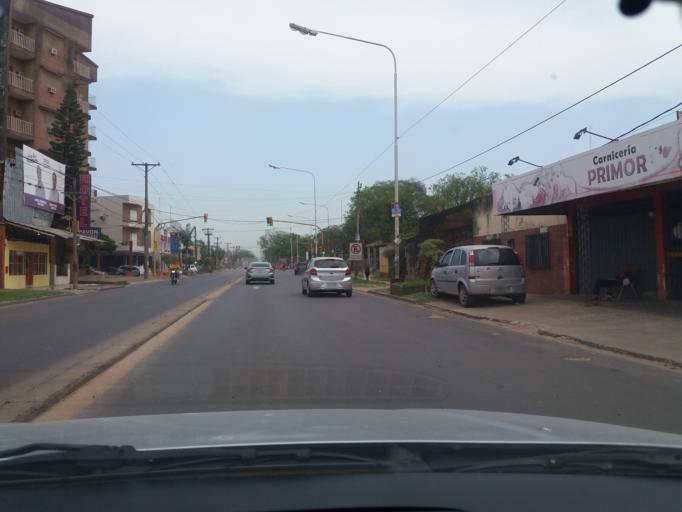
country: AR
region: Corrientes
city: Corrientes
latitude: -27.4994
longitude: -58.8144
